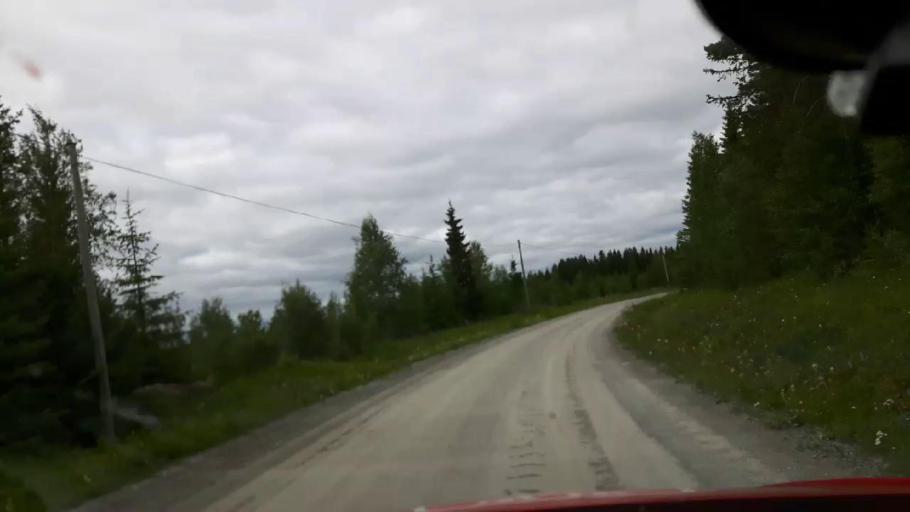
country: SE
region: Jaemtland
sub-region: OEstersunds Kommun
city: Brunflo
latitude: 63.0656
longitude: 14.8965
